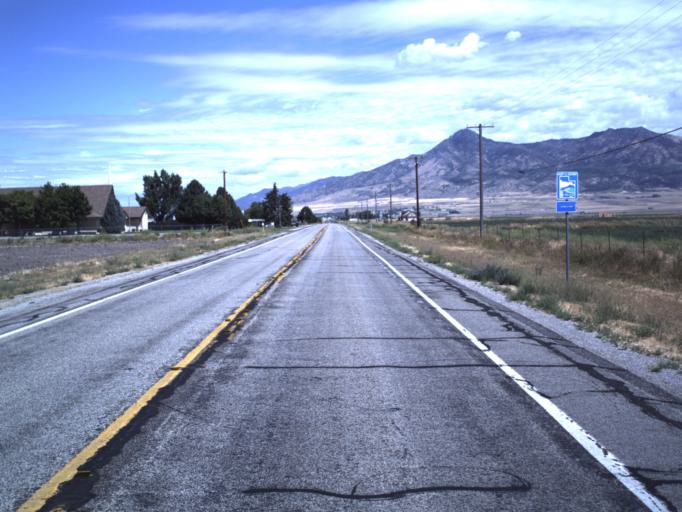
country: US
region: Utah
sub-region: Box Elder County
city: Garland
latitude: 41.8147
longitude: -112.1453
